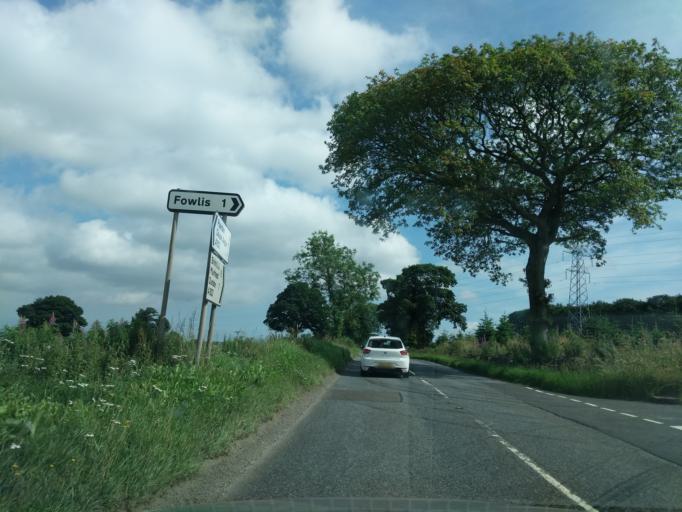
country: GB
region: Scotland
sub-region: Angus
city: Muirhead
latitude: 56.5018
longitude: -3.1116
